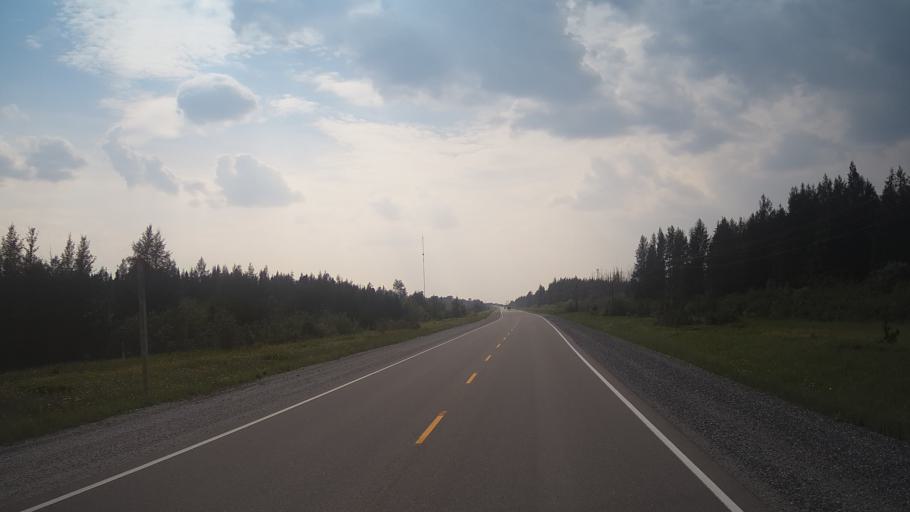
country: CA
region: Ontario
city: Kapuskasing
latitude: 49.5478
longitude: -82.9761
